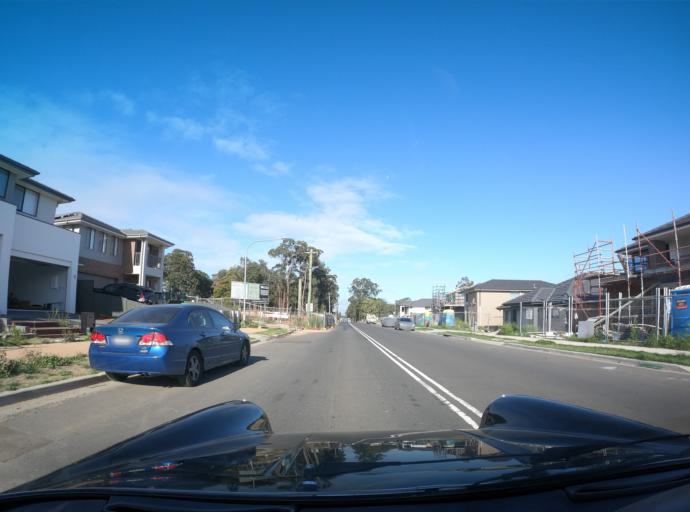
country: AU
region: New South Wales
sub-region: The Hills Shire
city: Beaumont Hills
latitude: -33.6843
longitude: 150.9555
